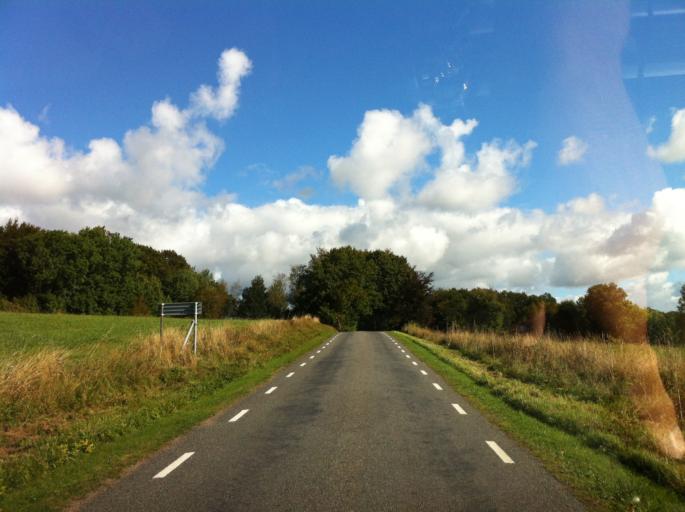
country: SE
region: Skane
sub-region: Horby Kommun
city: Hoerby
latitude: 55.7876
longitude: 13.7654
